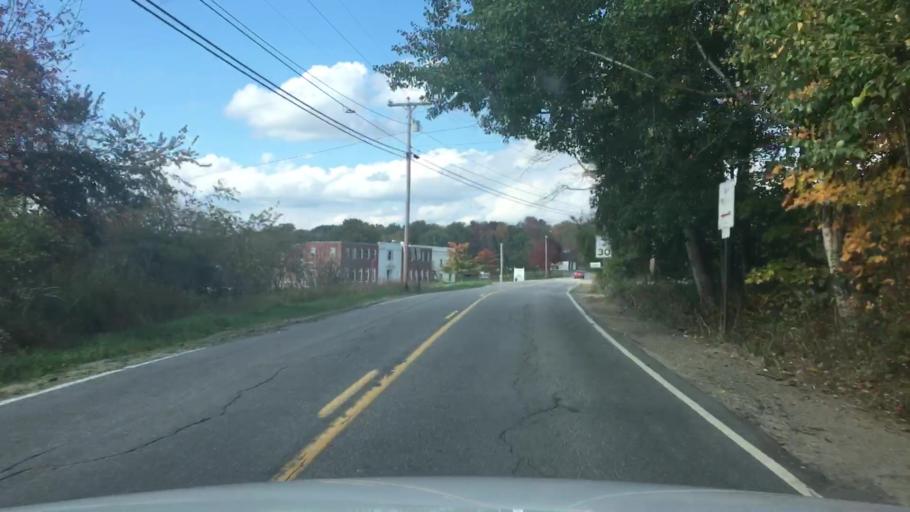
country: US
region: Maine
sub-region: Knox County
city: Union
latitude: 44.2102
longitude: -69.2632
